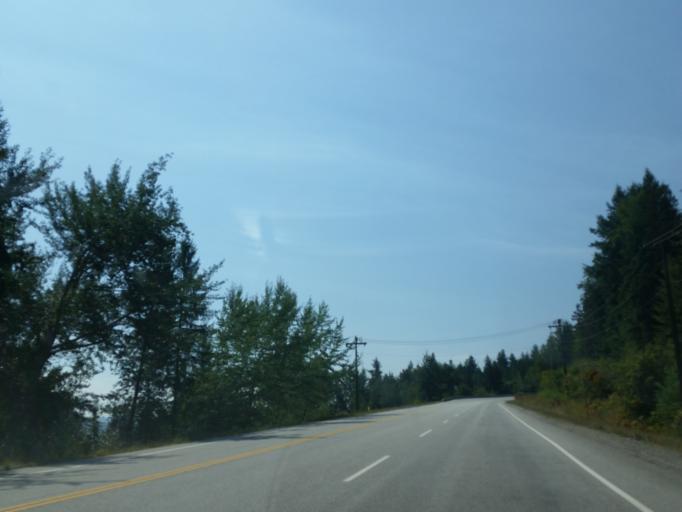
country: CA
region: British Columbia
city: Castlegar
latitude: 49.2922
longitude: -117.6565
